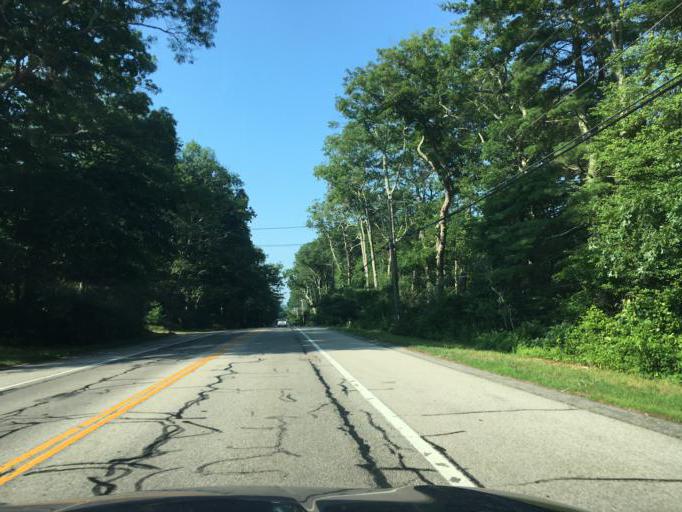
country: US
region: Rhode Island
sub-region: Washington County
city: Kingston
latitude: 41.5068
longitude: -71.5593
